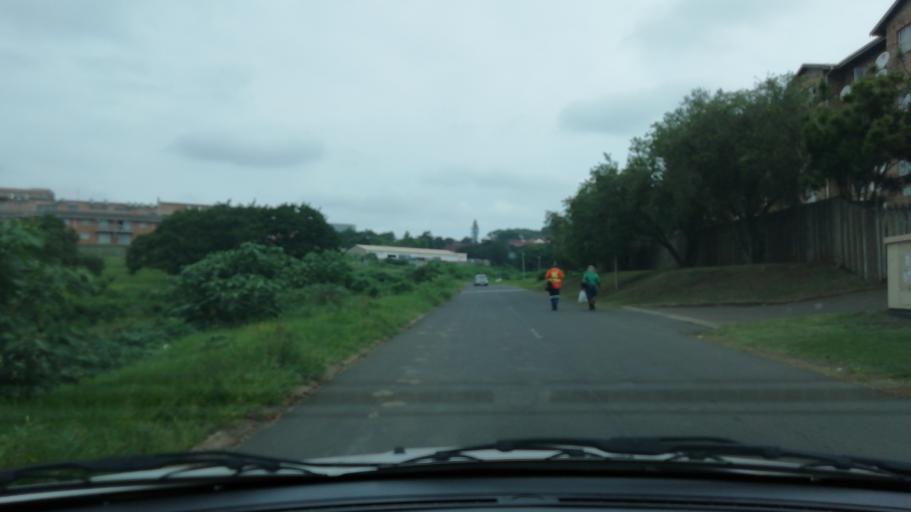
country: ZA
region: KwaZulu-Natal
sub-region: uThungulu District Municipality
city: Empangeni
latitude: -28.7406
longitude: 31.8854
